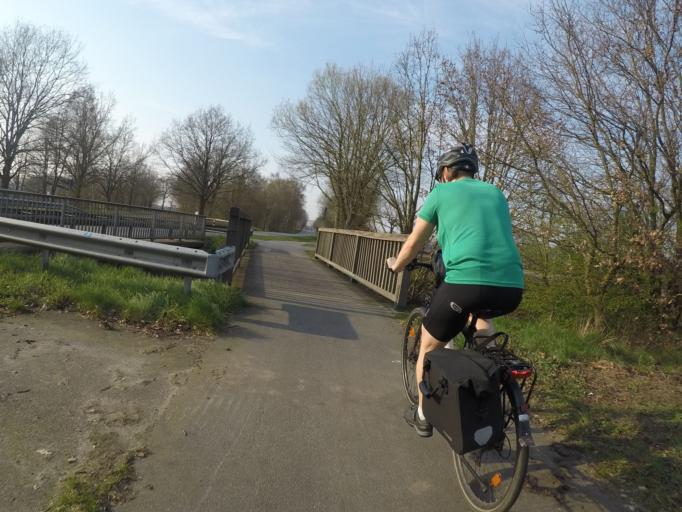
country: DE
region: Schleswig-Holstein
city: Wahlstedt
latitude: 53.9667
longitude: 10.1910
